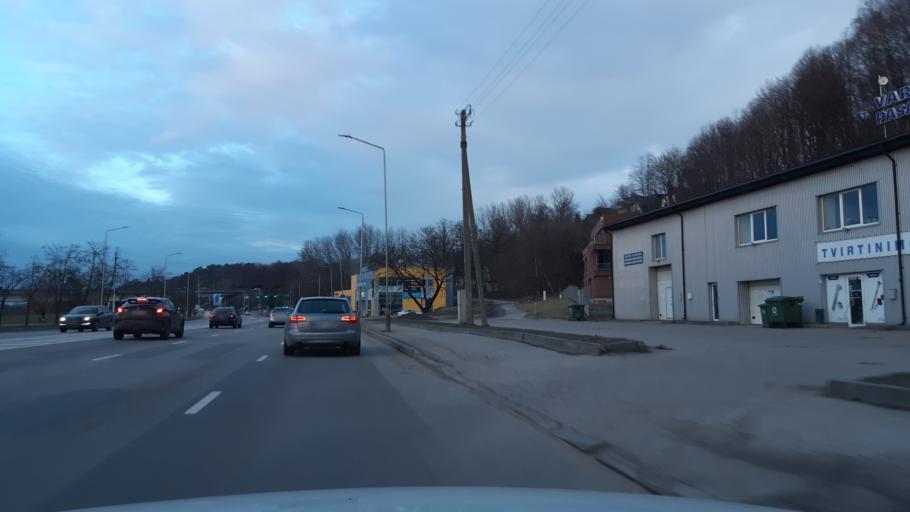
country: LT
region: Kauno apskritis
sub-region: Kaunas
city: Kaunas
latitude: 54.9108
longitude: 23.9089
